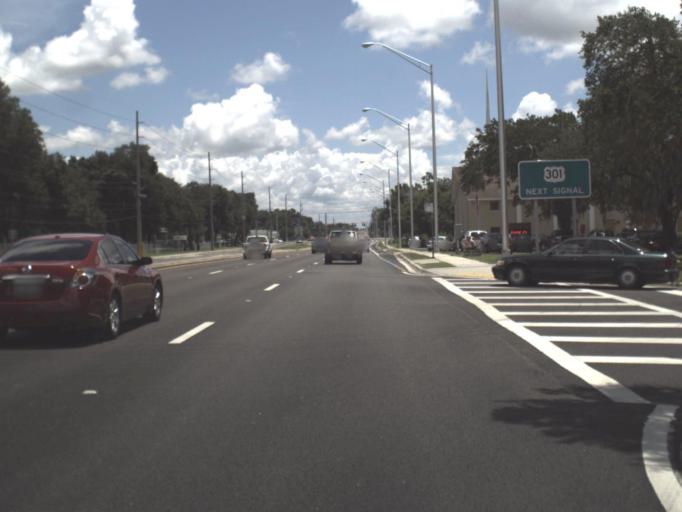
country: US
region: Florida
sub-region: Hillsborough County
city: East Lake-Orient Park
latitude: 27.9814
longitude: -82.3642
